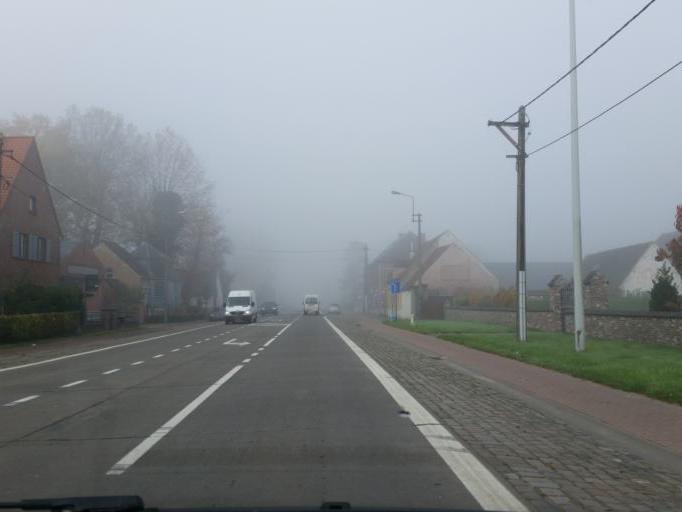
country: BE
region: Flanders
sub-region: Provincie Oost-Vlaanderen
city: Melle
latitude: 50.9923
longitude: 3.8284
